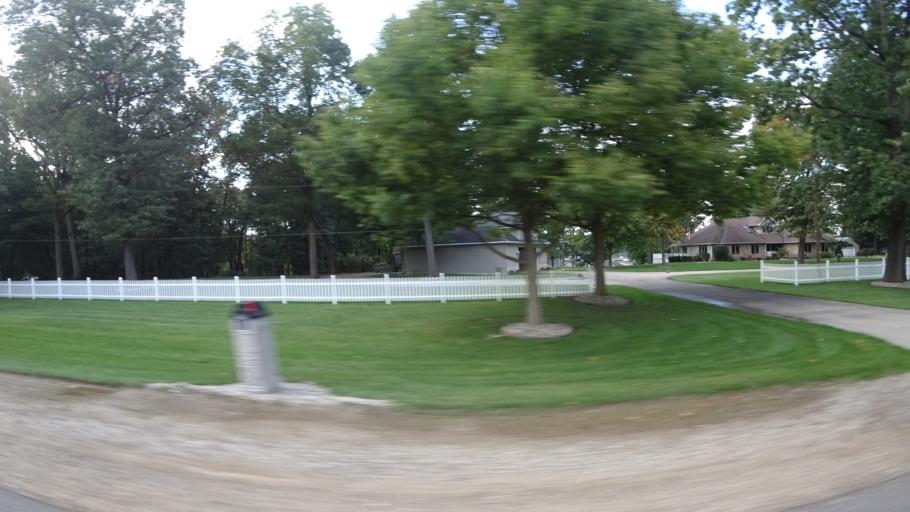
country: US
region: Michigan
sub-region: Saint Joseph County
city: Centreville
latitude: 41.9812
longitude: -85.5671
